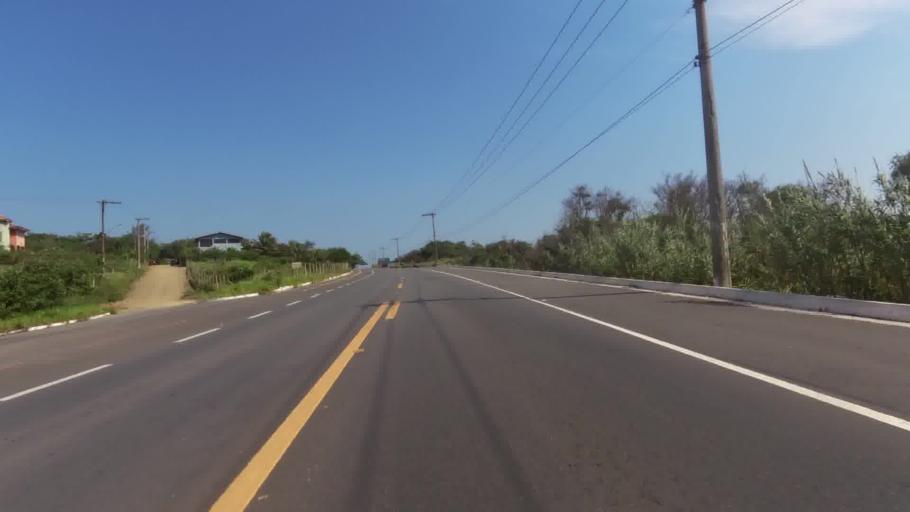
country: BR
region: Espirito Santo
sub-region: Piuma
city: Piuma
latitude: -20.8169
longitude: -40.6152
